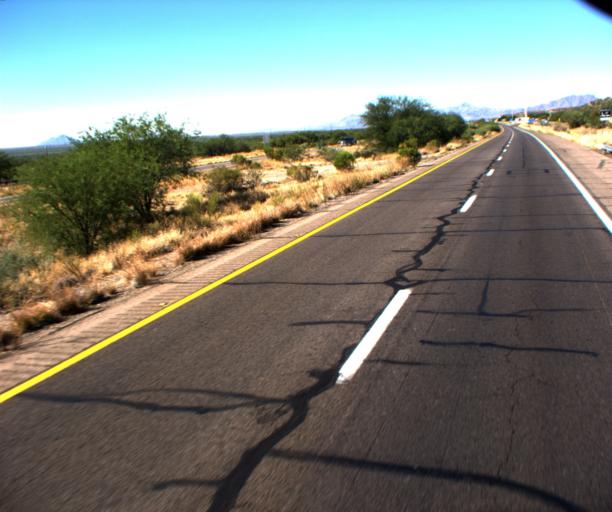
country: US
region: Arizona
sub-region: Pima County
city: Arivaca Junction
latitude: 31.7784
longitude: -111.0292
